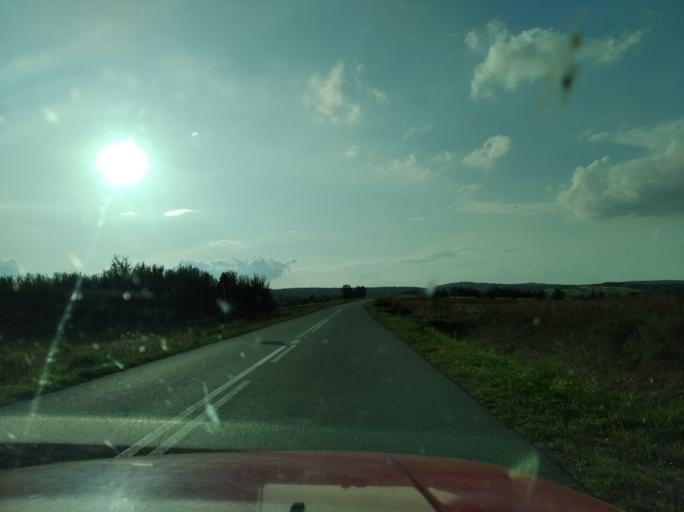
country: PL
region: Subcarpathian Voivodeship
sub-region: Powiat jaroslawski
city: Jodlowka
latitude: 49.8825
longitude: 22.4607
